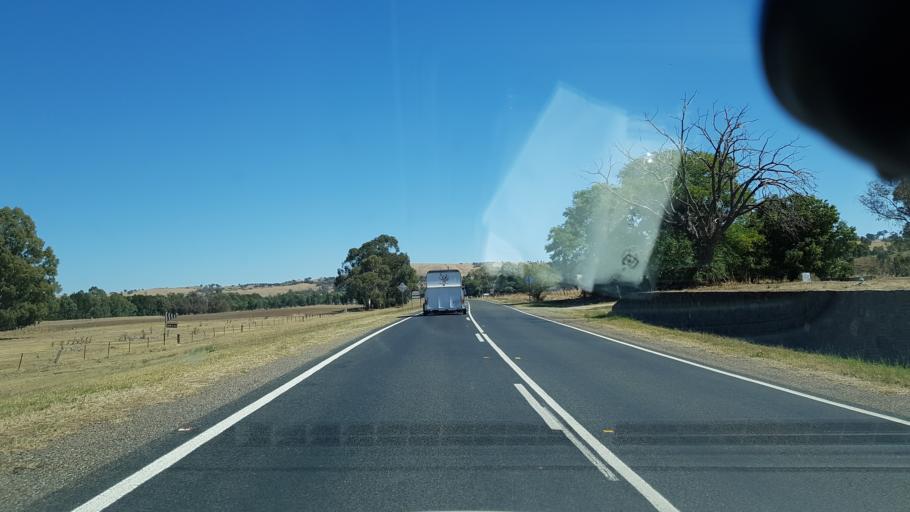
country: AU
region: New South Wales
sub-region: Gundagai
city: Gundagai
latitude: -34.8225
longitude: 148.3468
